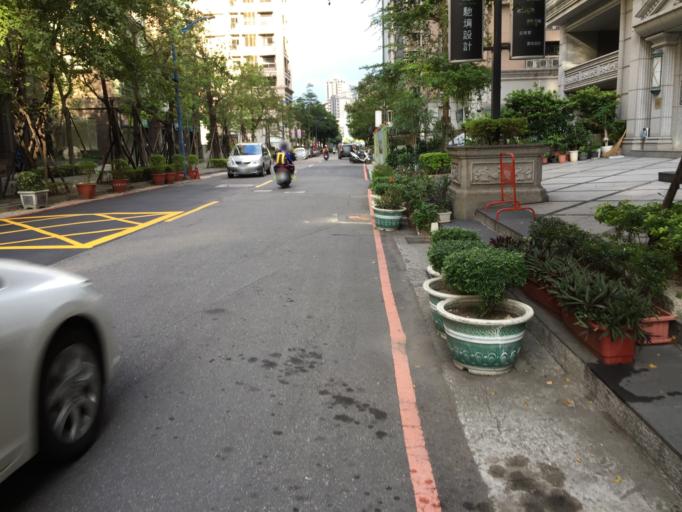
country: TW
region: Taipei
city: Taipei
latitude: 25.0857
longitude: 121.4949
